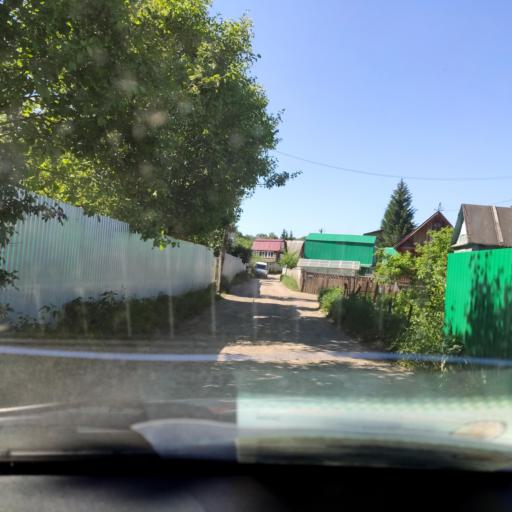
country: RU
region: Bashkortostan
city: Ufa
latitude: 54.7863
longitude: 56.1848
